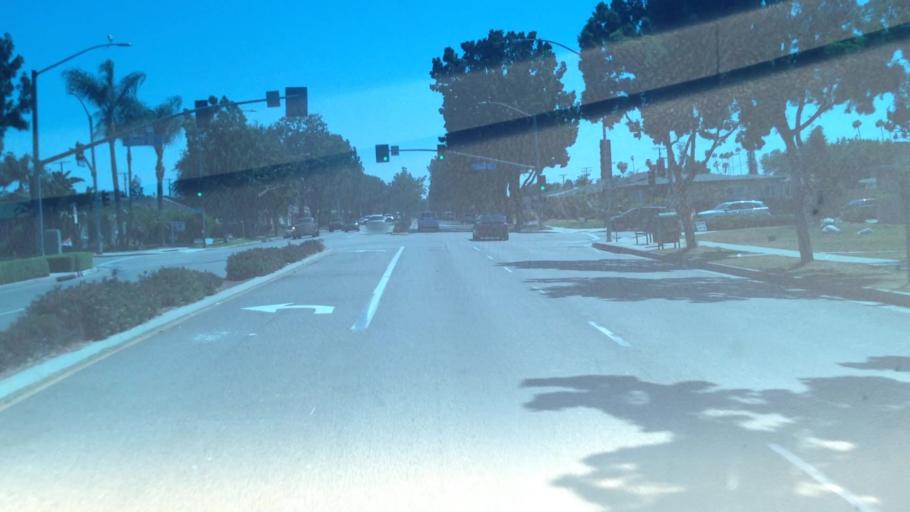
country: US
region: California
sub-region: Los Angeles County
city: Downey
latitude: 33.9603
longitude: -118.1249
